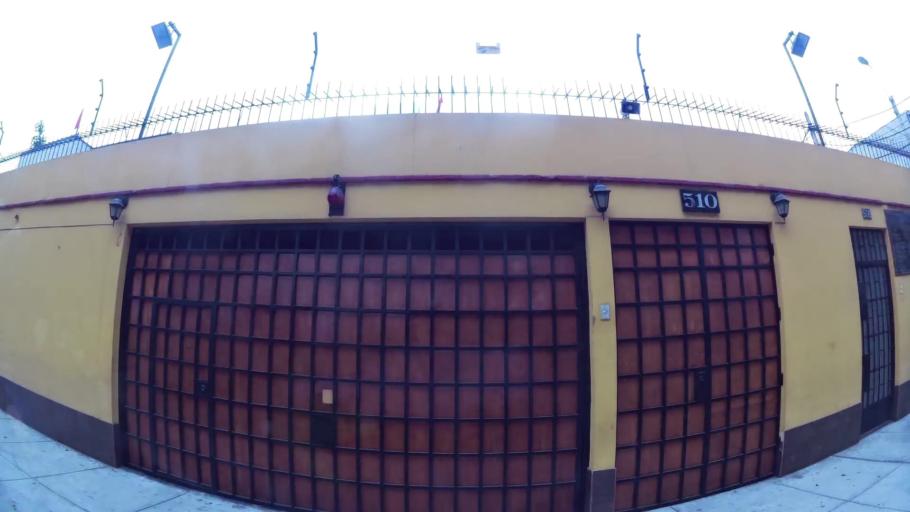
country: PE
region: Lima
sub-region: Lima
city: Surco
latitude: -12.1167
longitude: -77.0066
